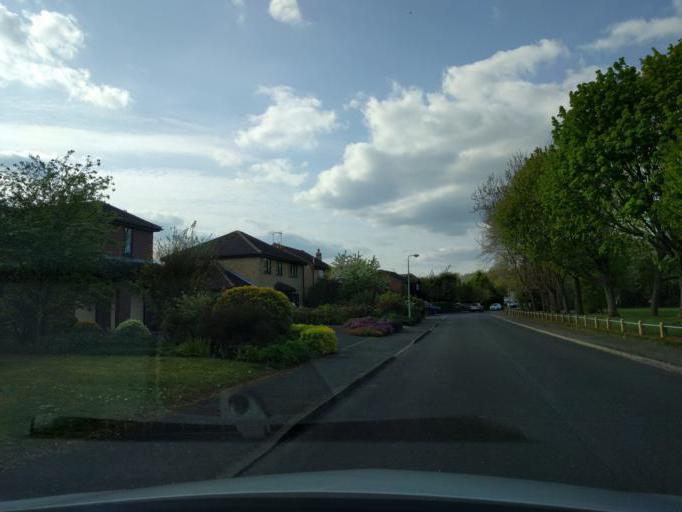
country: GB
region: England
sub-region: Suffolk
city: Bury St Edmunds
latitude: 52.2431
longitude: 0.7437
